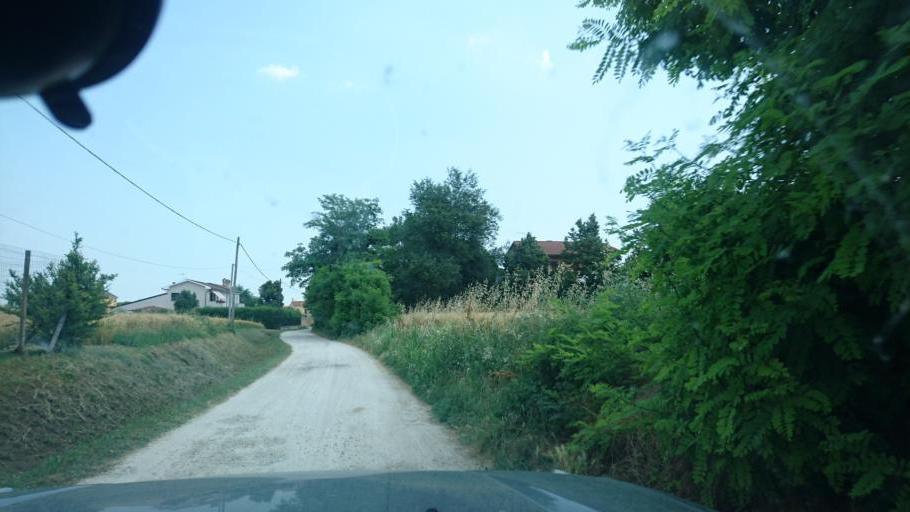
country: IT
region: Veneto
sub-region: Provincia di Padova
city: Monselice
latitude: 45.2215
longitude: 11.7366
